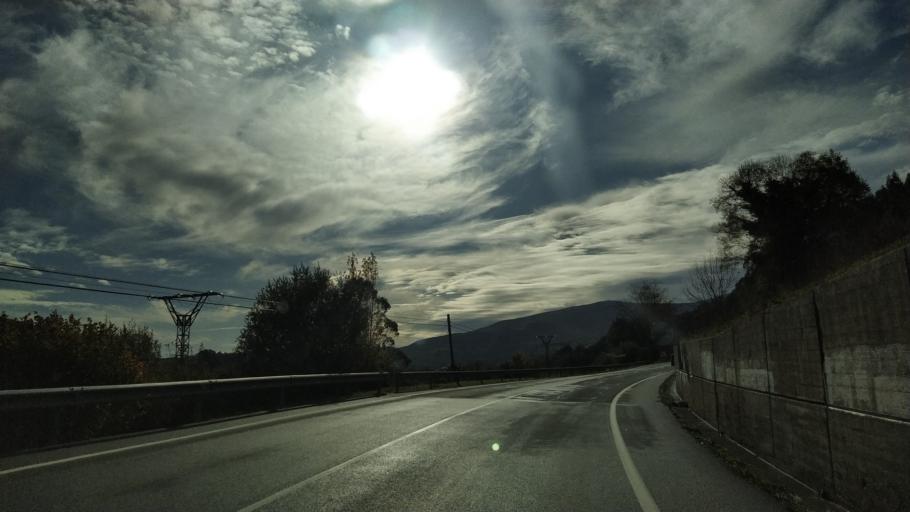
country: ES
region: Cantabria
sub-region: Provincia de Cantabria
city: Santiurde de Toranzo
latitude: 43.2440
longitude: -3.9469
